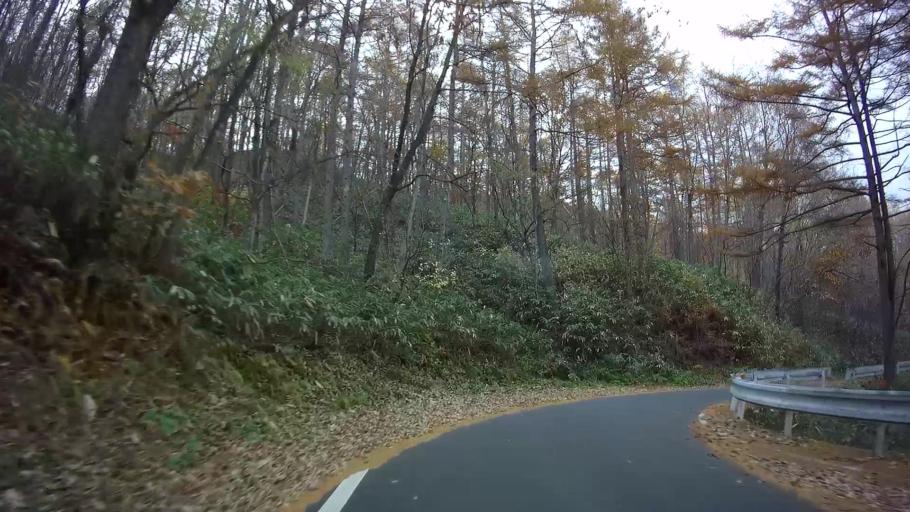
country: JP
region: Gunma
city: Nakanojomachi
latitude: 36.6727
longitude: 138.6683
